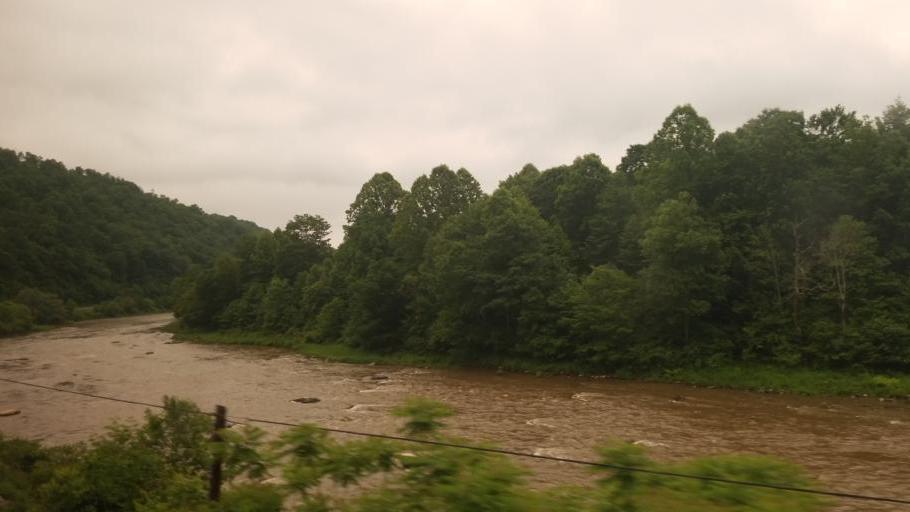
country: US
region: Pennsylvania
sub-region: Somerset County
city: Milford
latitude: 39.8830
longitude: -79.2294
